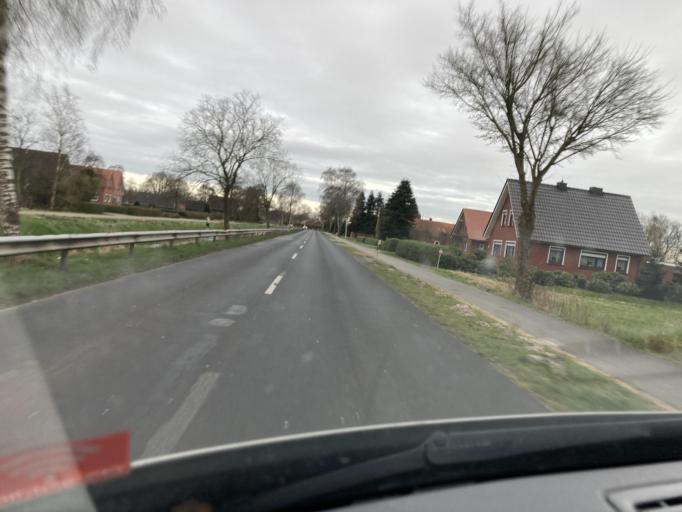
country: DE
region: Lower Saxony
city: Papenburg
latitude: 53.1307
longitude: 7.4875
